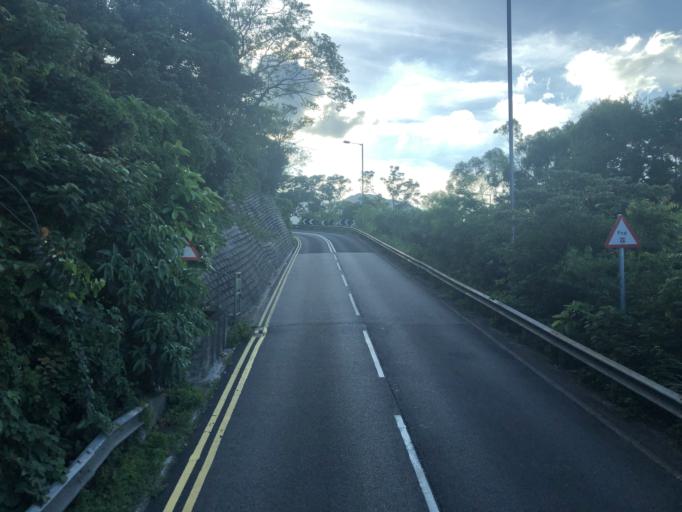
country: HK
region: Sai Kung
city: Sai Kung
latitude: 22.3438
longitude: 114.2537
